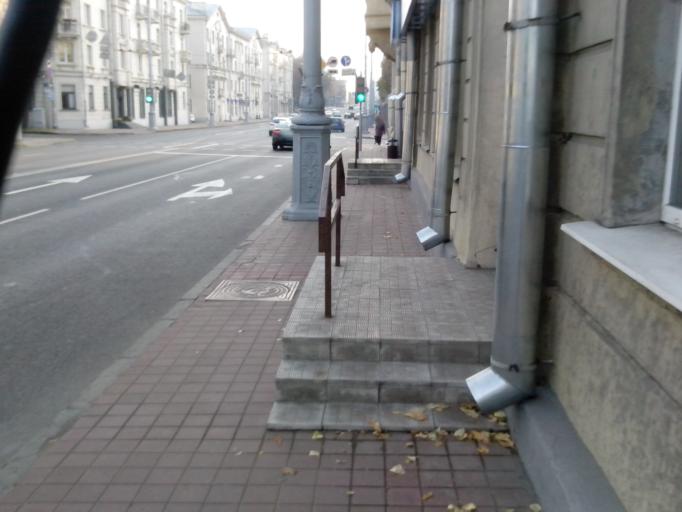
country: BY
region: Minsk
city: Minsk
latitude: 53.9140
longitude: 27.5617
